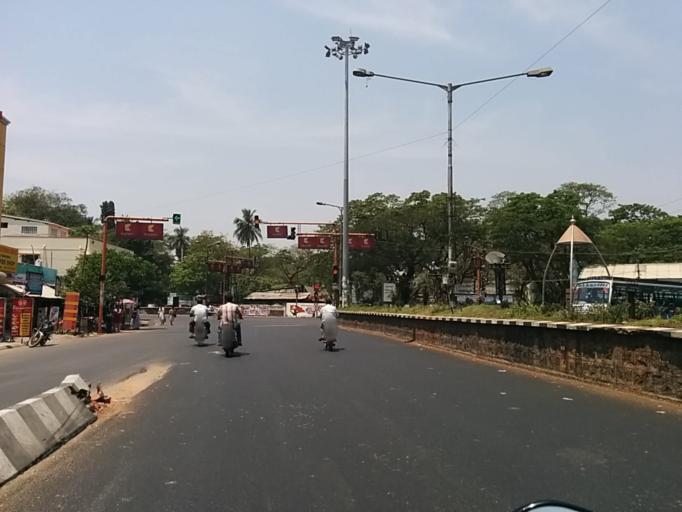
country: IN
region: Pondicherry
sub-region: Puducherry
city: Puducherry
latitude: 11.9326
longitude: 79.8125
